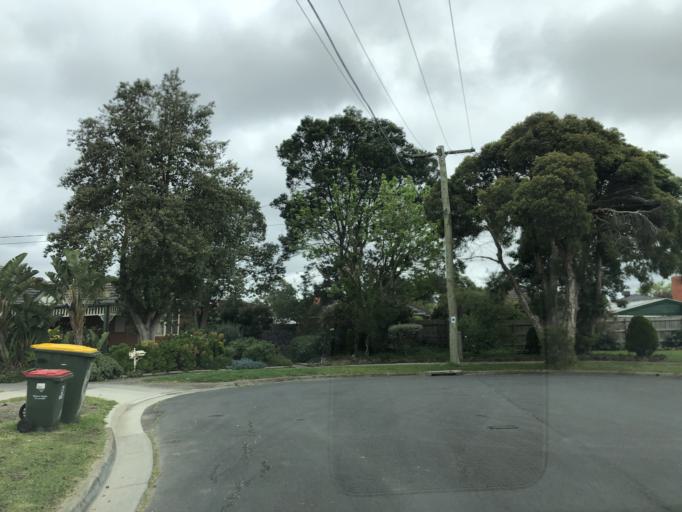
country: AU
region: Victoria
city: Burwood East
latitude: -37.8585
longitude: 145.1463
